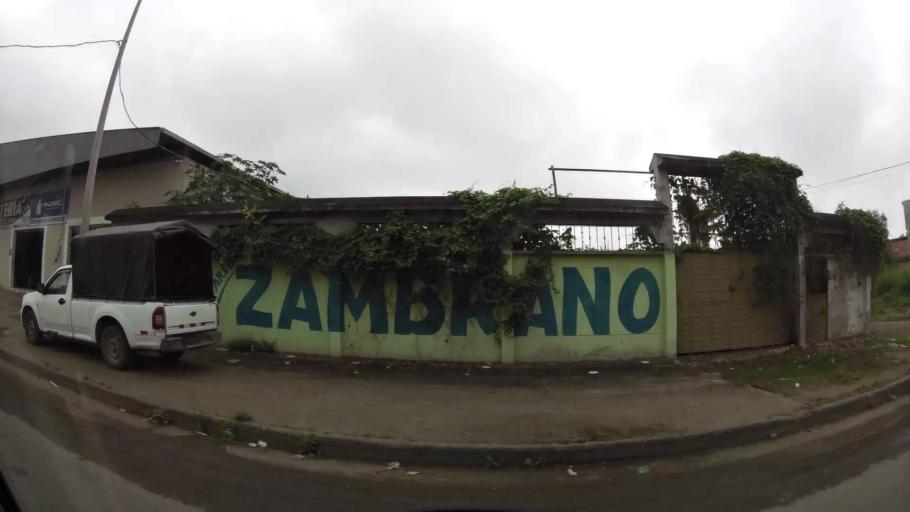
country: EC
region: El Oro
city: Pasaje
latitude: -3.3270
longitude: -79.8221
